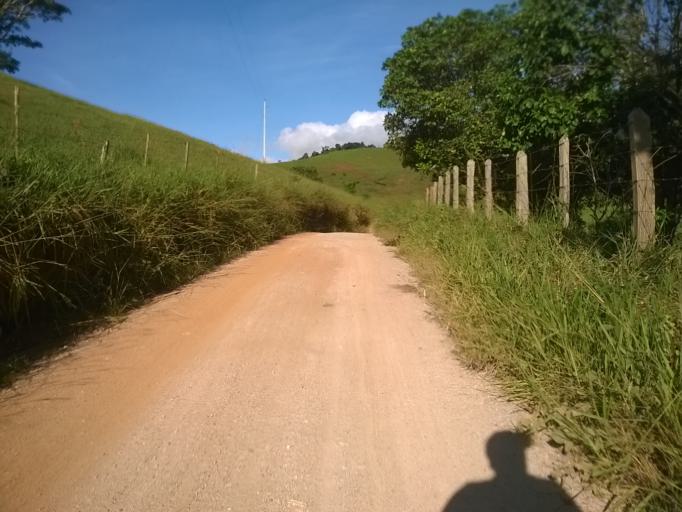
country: BR
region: Minas Gerais
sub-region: Uba
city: Uba
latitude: -21.0892
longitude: -43.0114
